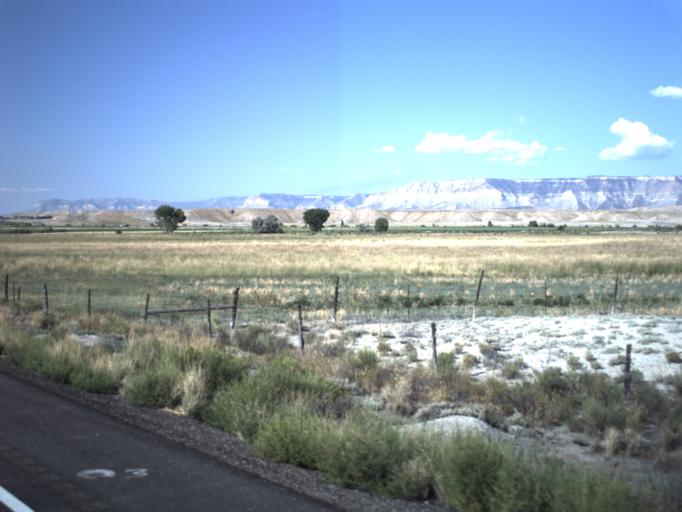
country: US
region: Utah
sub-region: Emery County
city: Huntington
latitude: 39.2777
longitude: -110.9763
